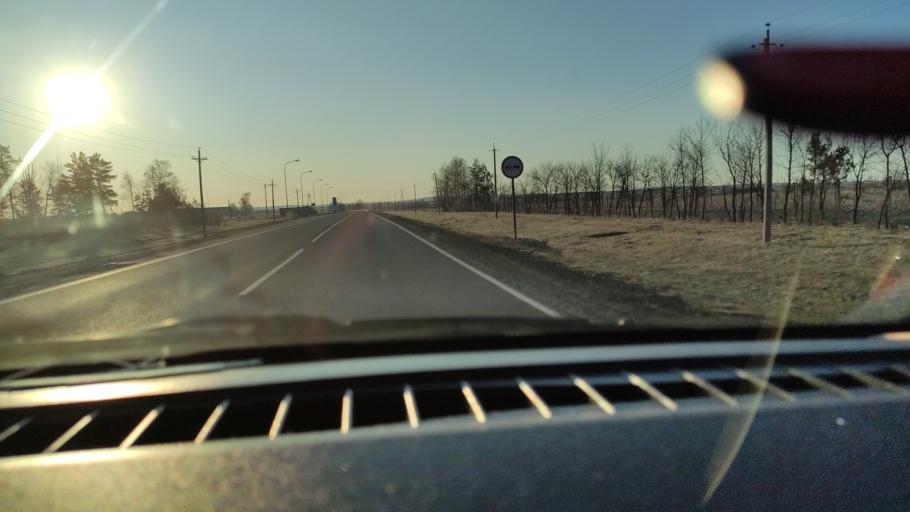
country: RU
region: Saratov
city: Sennoy
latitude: 52.1508
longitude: 46.9745
